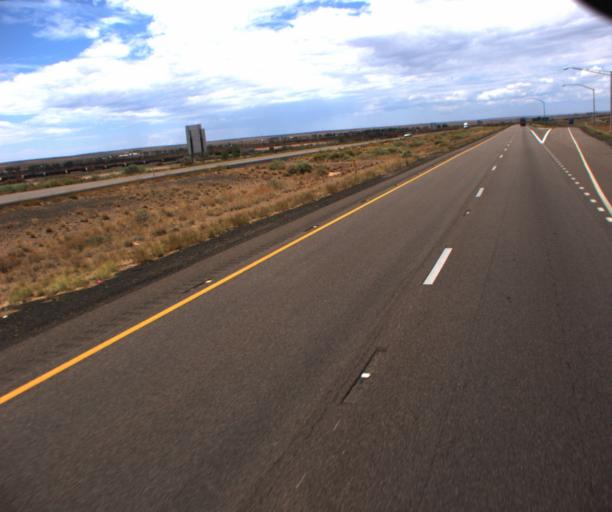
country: US
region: Arizona
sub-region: Navajo County
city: Holbrook
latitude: 34.9083
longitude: -110.1802
